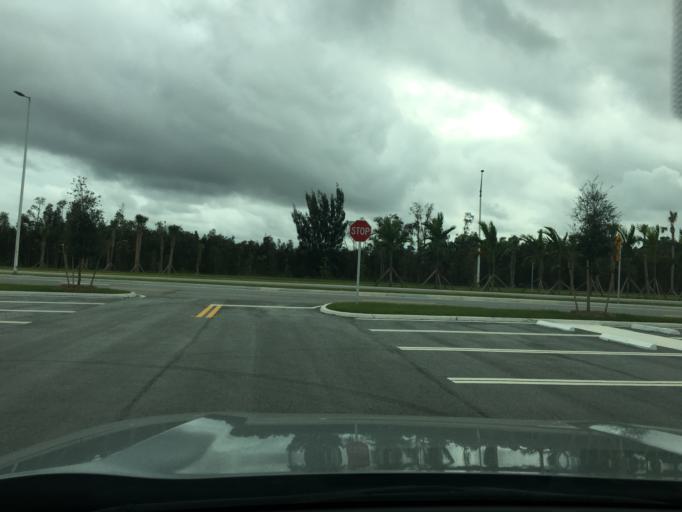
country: US
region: Florida
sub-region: Miami-Dade County
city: Palm Springs North
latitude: 25.9429
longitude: -80.3559
